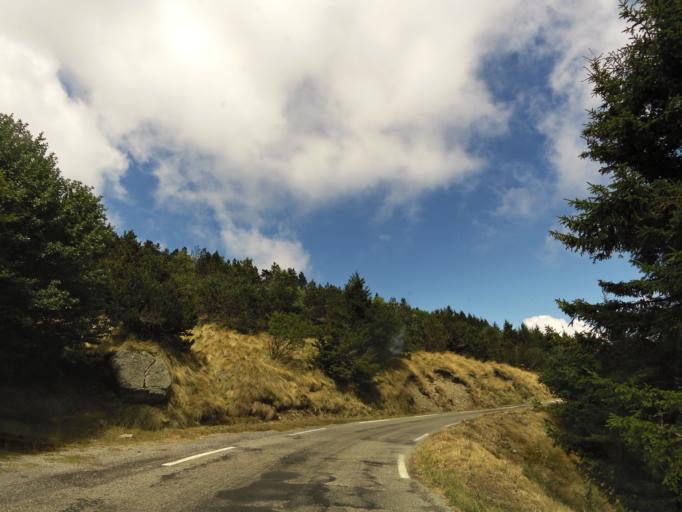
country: FR
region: Languedoc-Roussillon
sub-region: Departement du Gard
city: Valleraugue
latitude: 44.1190
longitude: 3.5751
